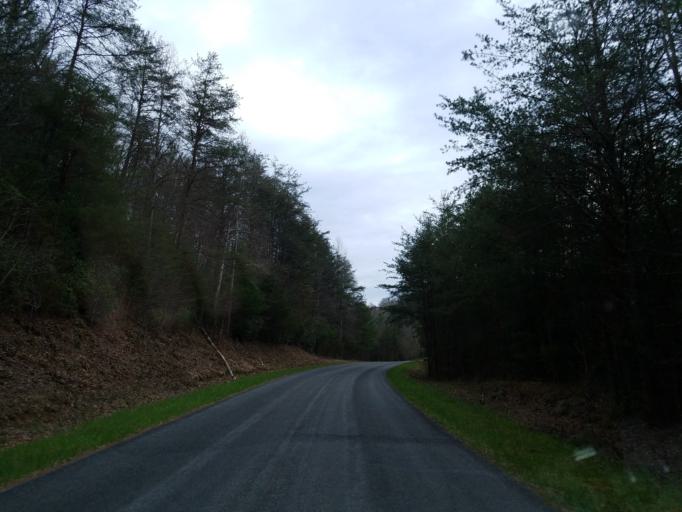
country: US
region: Georgia
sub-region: Fannin County
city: Blue Ridge
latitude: 34.7294
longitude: -84.2847
